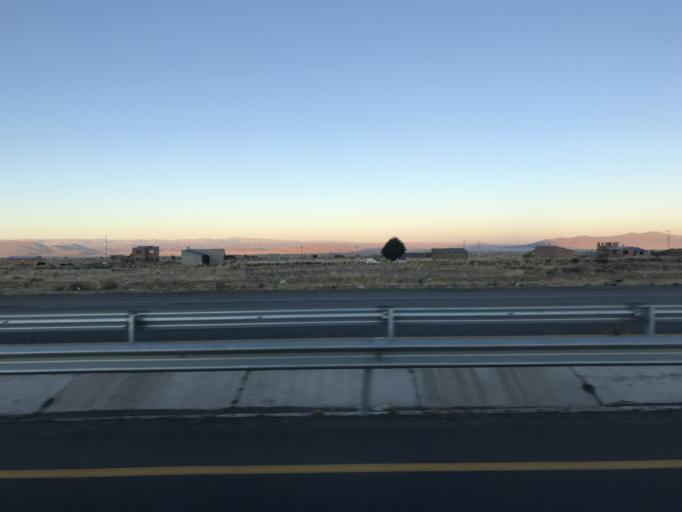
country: BO
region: La Paz
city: Batallas
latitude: -16.3526
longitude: -68.4010
